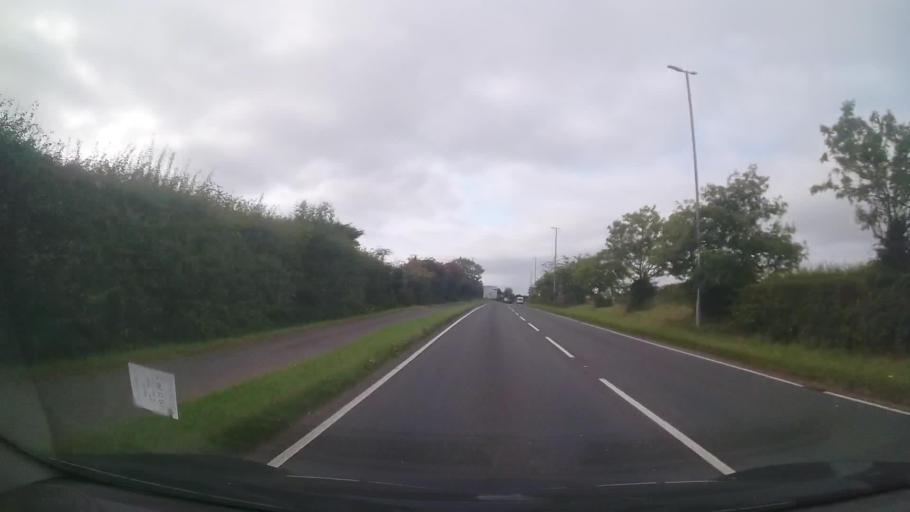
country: GB
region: Wales
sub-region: Pembrokeshire
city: Neyland
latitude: 51.7169
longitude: -4.9502
